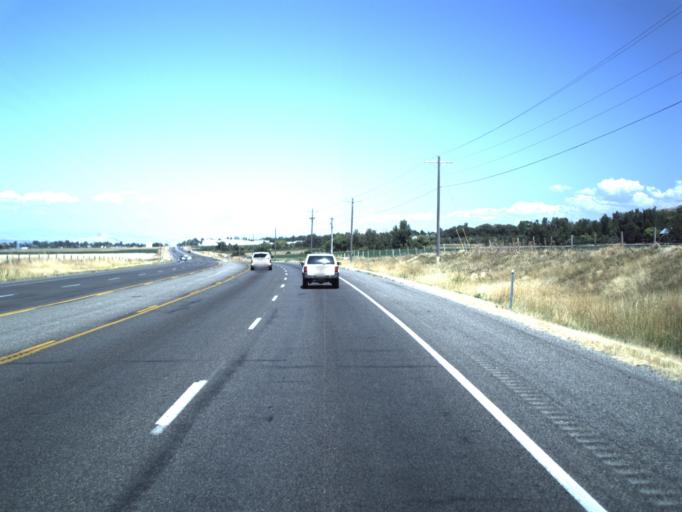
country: US
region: Utah
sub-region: Cache County
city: Richmond
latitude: 41.8905
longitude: -111.8151
